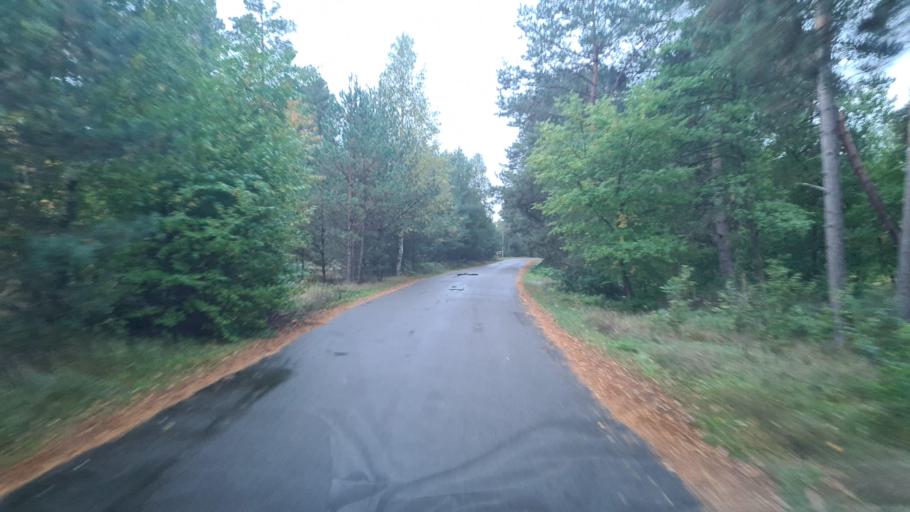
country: DE
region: Brandenburg
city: Munchehofe
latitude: 52.1368
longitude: 13.9413
